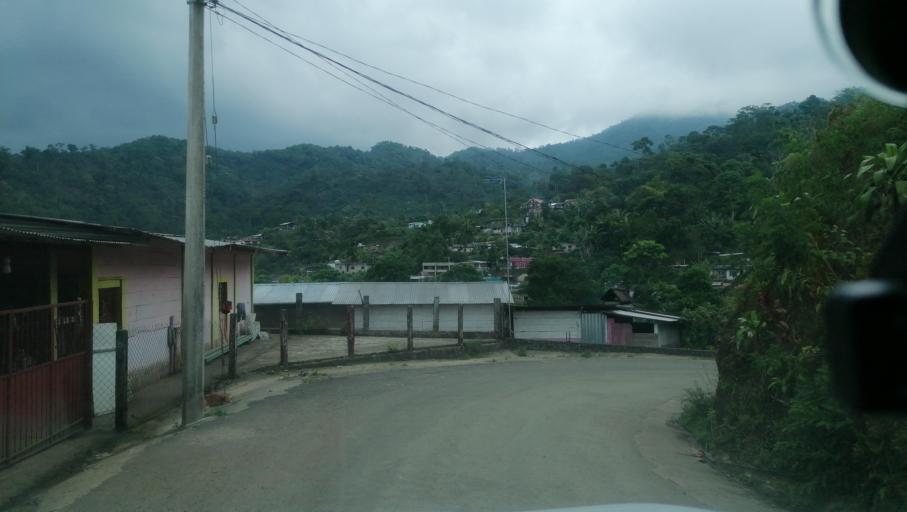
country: MX
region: Chiapas
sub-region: Cacahoatan
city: Benito Juarez
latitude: 15.0717
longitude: -92.1687
